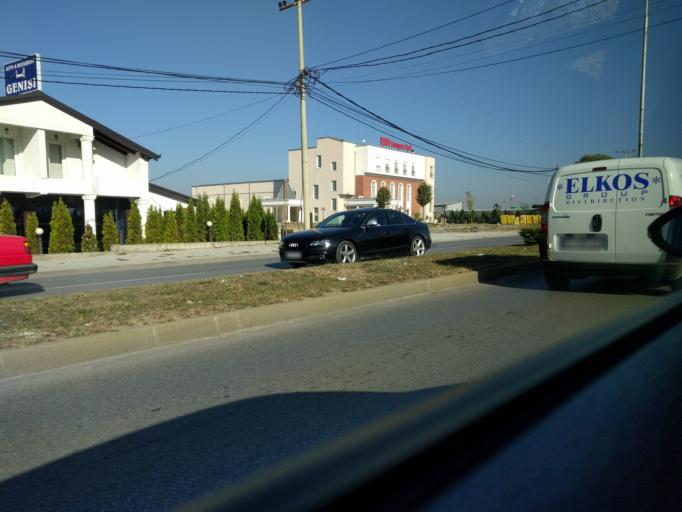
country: XK
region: Prizren
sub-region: Prizren
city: Prizren
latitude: 42.2324
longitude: 20.7574
